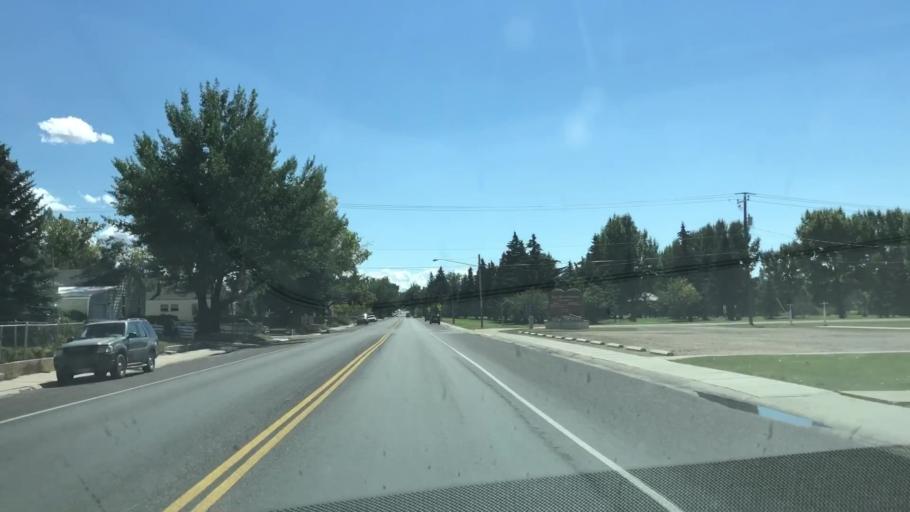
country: US
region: Wyoming
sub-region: Albany County
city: Laramie
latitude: 41.3235
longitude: -105.5843
